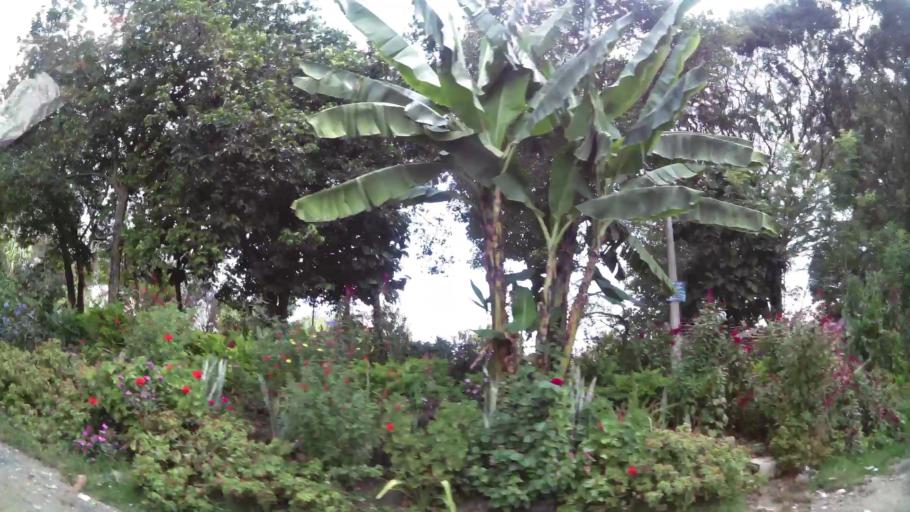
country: CO
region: Valle del Cauca
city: Cali
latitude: 3.4764
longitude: -76.4791
